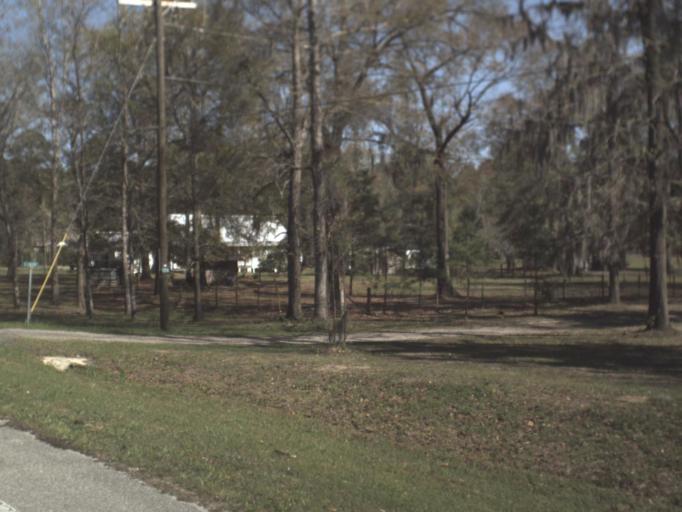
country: US
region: Florida
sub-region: Jefferson County
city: Monticello
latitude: 30.3867
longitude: -84.0095
